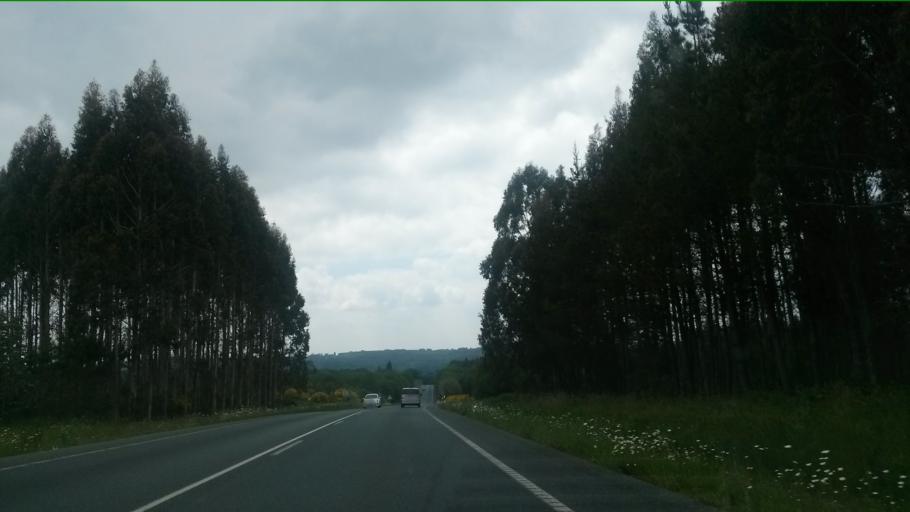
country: ES
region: Galicia
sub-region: Provincia da Coruna
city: Curtis
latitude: 43.1193
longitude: -8.0868
